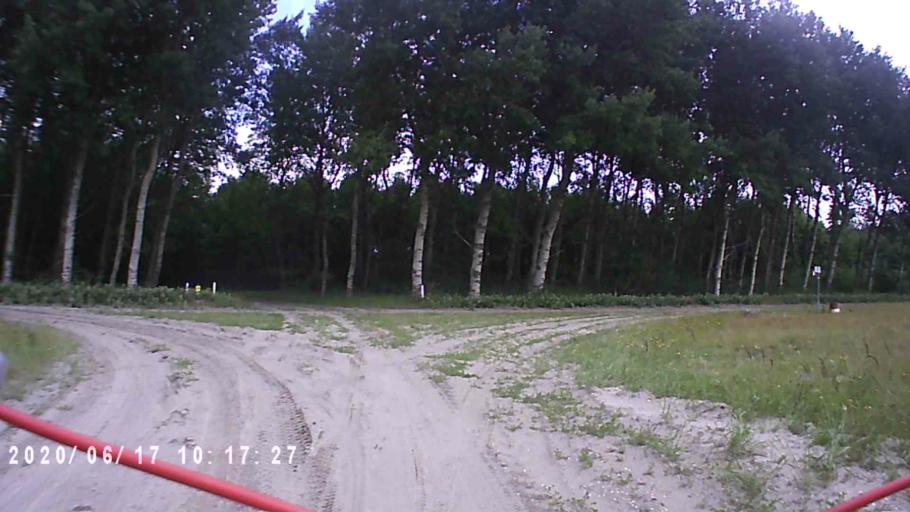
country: NL
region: Groningen
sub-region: Gemeente De Marne
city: Ulrum
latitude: 53.3842
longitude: 6.2587
